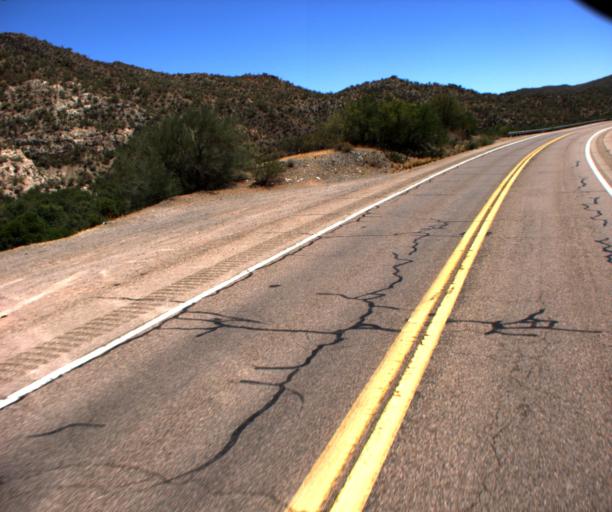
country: US
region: Arizona
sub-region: Pinal County
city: Kearny
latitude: 33.0343
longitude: -110.7296
